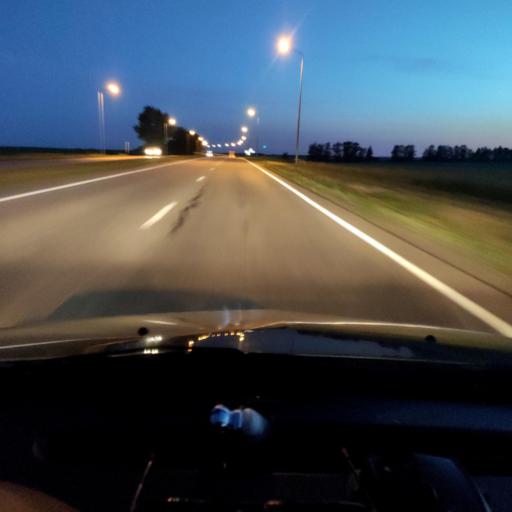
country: RU
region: Belgorod
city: Skorodnoye
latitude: 51.1745
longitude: 37.3291
